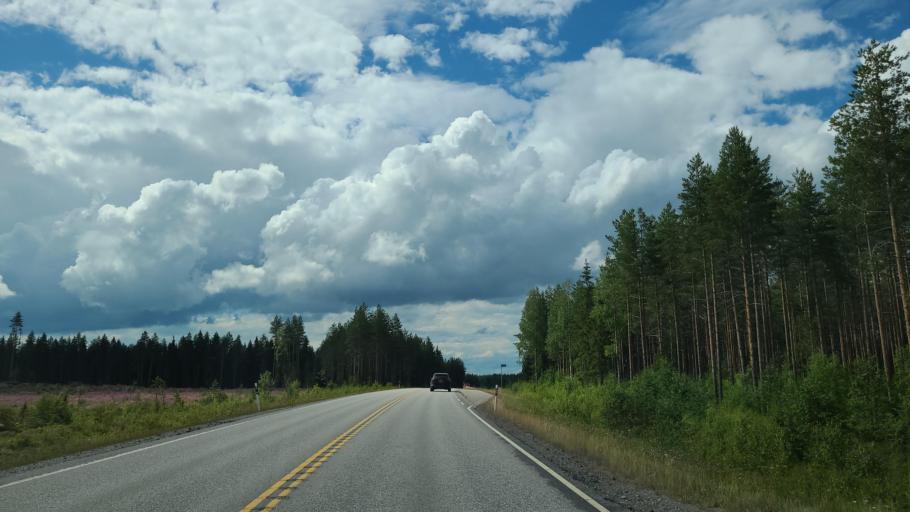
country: FI
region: Central Finland
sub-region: Jyvaeskylae
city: Hankasalmi
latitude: 62.3914
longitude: 26.6336
